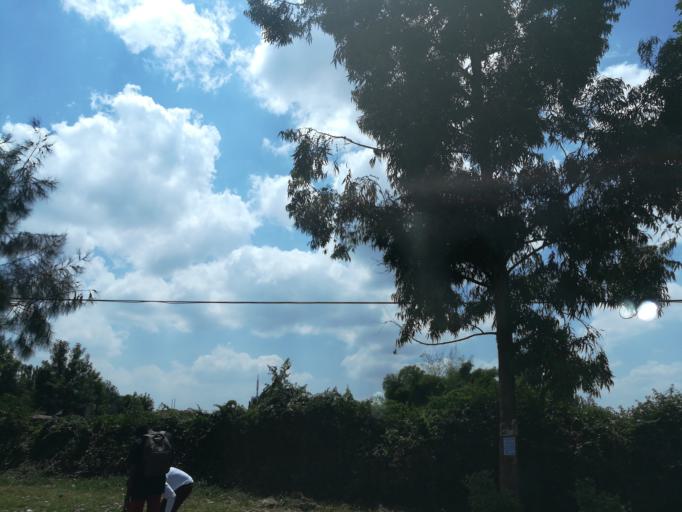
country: KE
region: Nairobi Area
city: Nairobi
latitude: -1.3144
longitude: 36.8080
